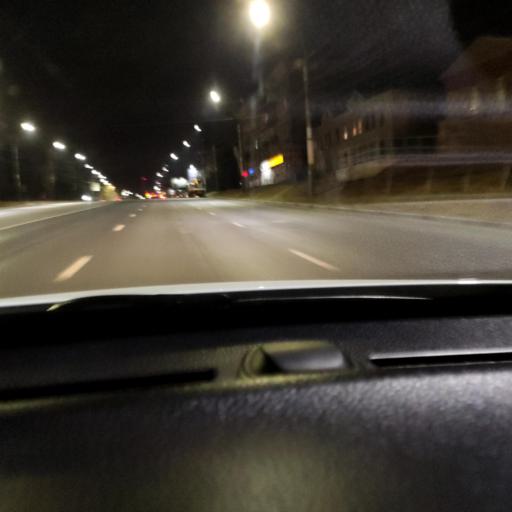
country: RU
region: Voronezj
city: Voronezh
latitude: 51.6434
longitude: 39.2017
